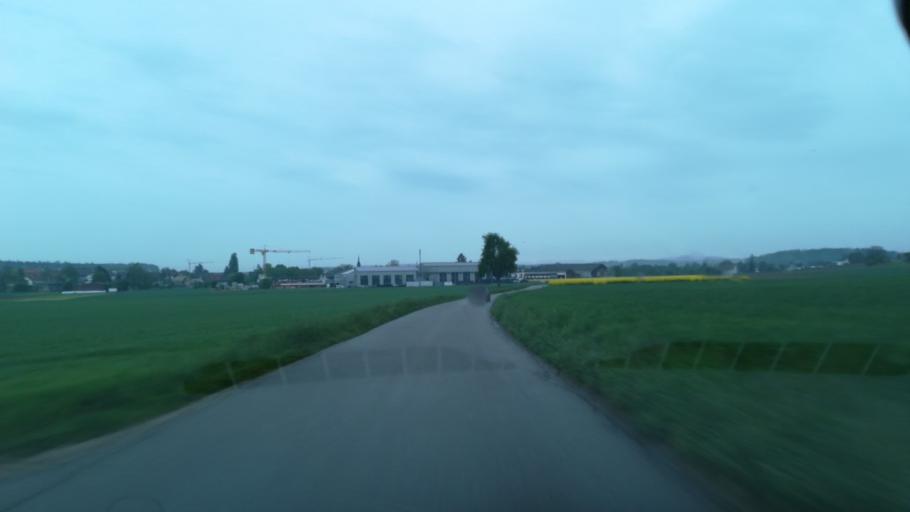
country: CH
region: Zurich
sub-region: Bezirk Buelach
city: End-Hoeri
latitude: 47.5138
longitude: 8.5016
